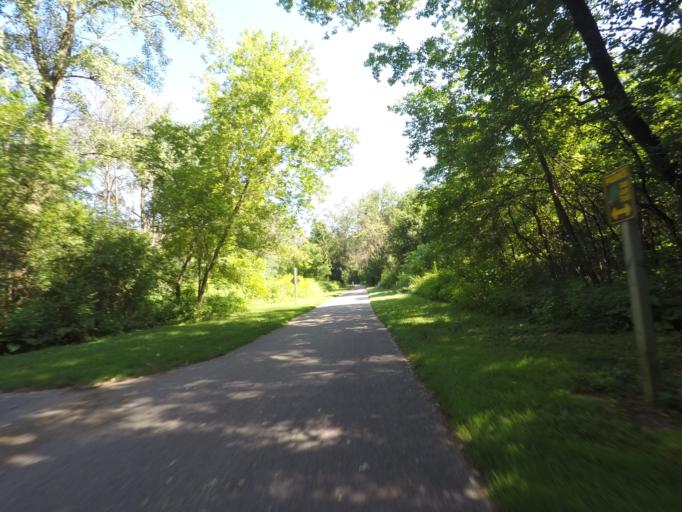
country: US
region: Wisconsin
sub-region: Waukesha County
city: Elm Grove
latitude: 43.0314
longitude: -88.0681
